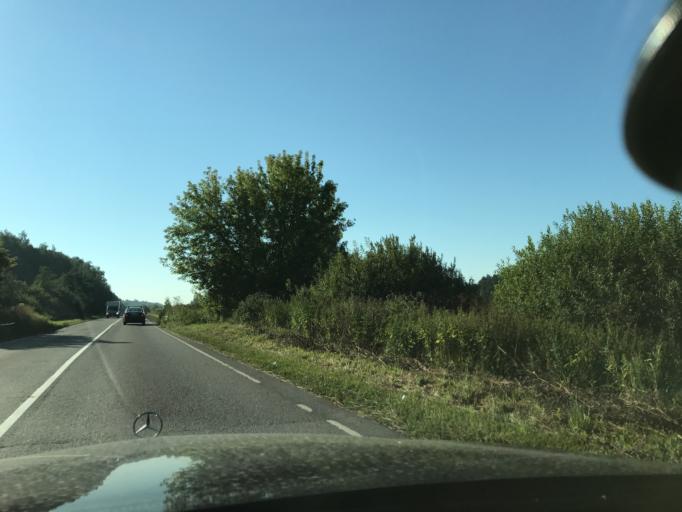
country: RU
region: Moskovskaya
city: Bakhchivandzhi
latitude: 55.8599
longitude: 38.0596
